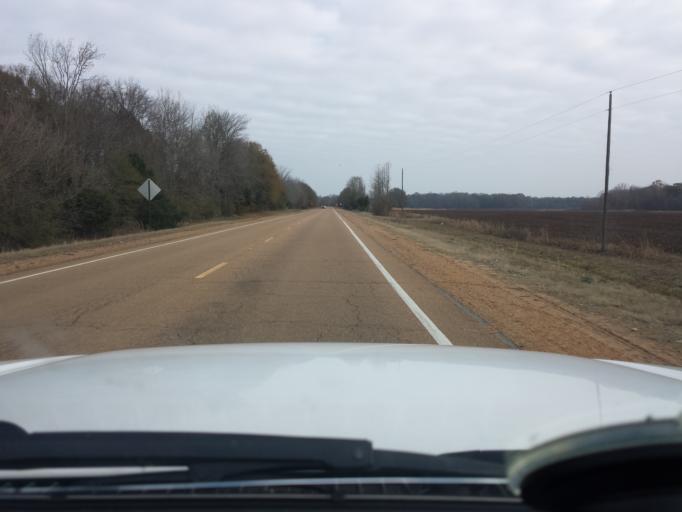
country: US
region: Mississippi
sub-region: Yazoo County
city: Yazoo City
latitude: 32.8010
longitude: -90.2253
